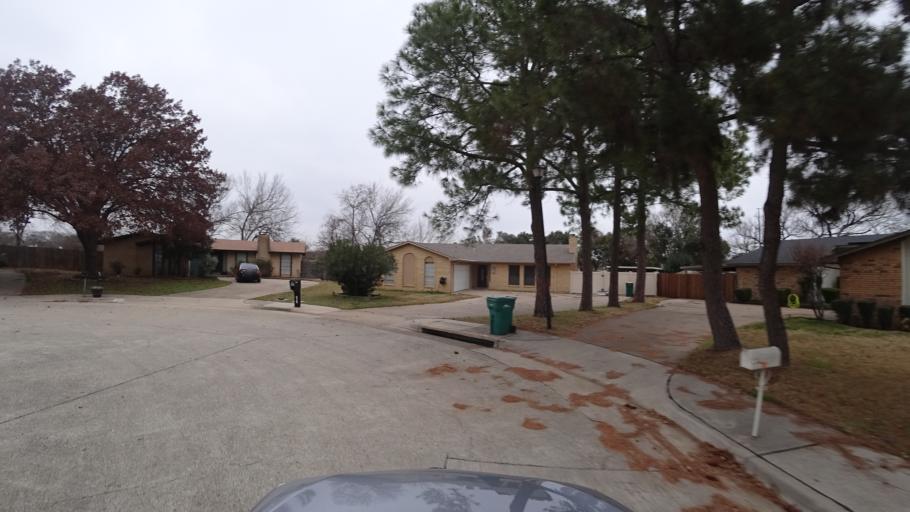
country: US
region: Texas
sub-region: Denton County
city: Highland Village
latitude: 33.0527
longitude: -97.0365
